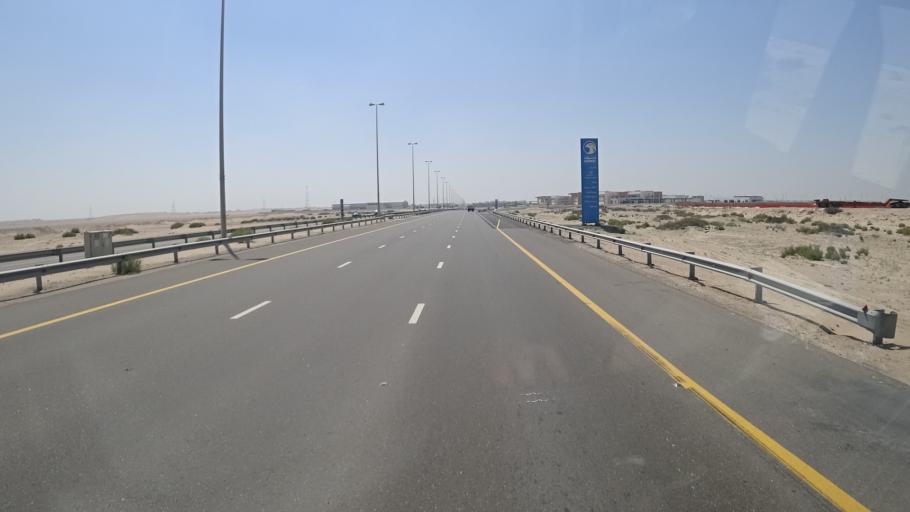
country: AE
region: Abu Dhabi
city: Abu Dhabi
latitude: 24.3185
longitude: 54.6820
